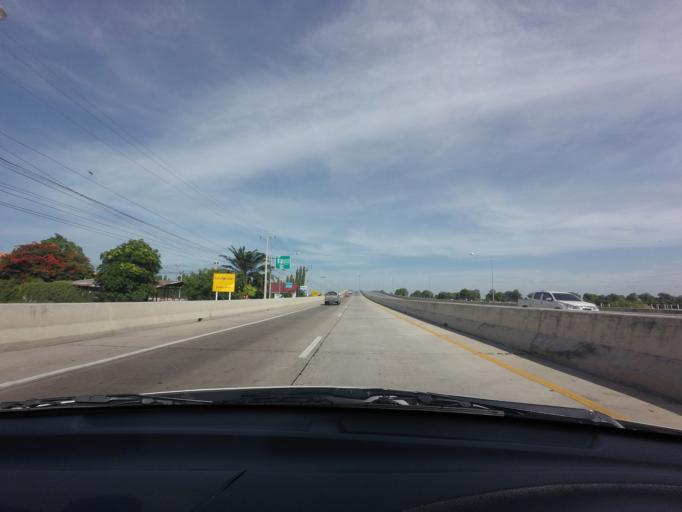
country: TH
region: Suphan Buri
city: Suphan Buri
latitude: 14.4522
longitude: 100.0929
